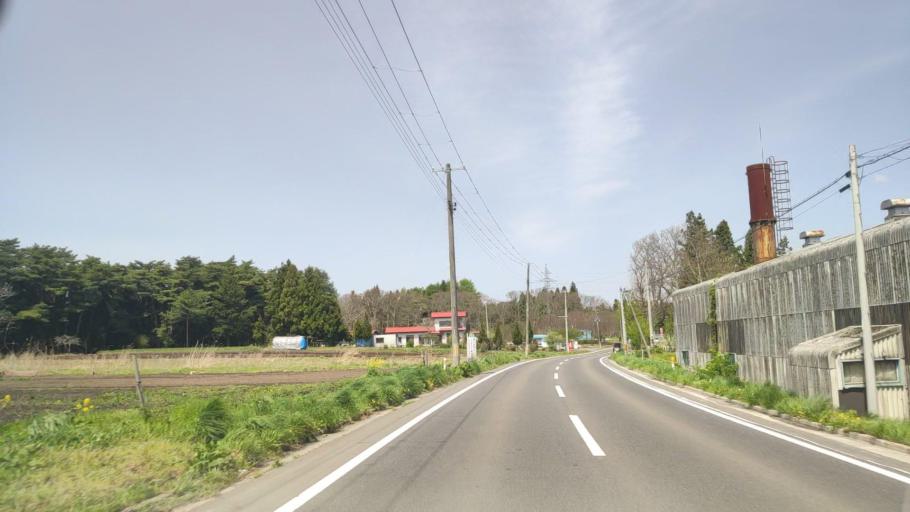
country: JP
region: Aomori
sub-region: Hachinohe Shi
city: Uchimaru
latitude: 40.5325
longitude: 141.4034
